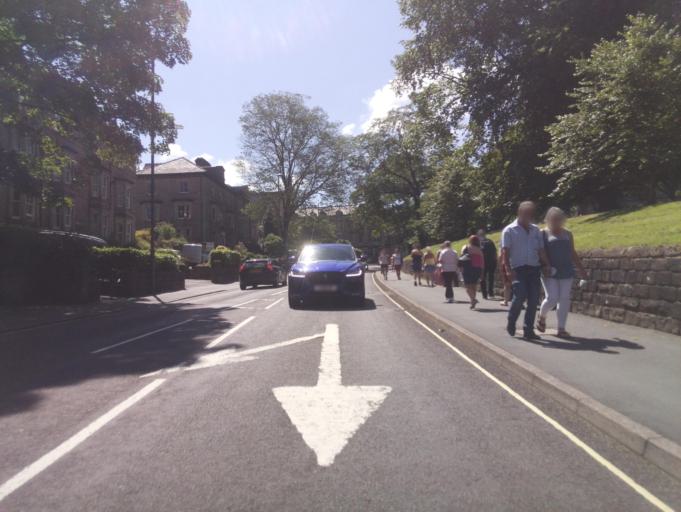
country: GB
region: England
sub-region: Derbyshire
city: Buxton
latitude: 53.2581
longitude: -1.9128
